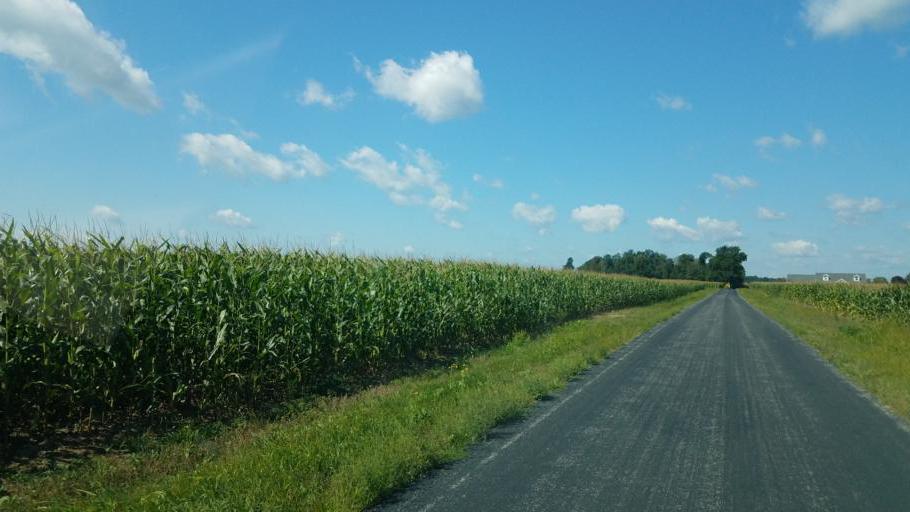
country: US
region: Ohio
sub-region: Wyandot County
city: Carey
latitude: 40.9780
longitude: -83.3307
